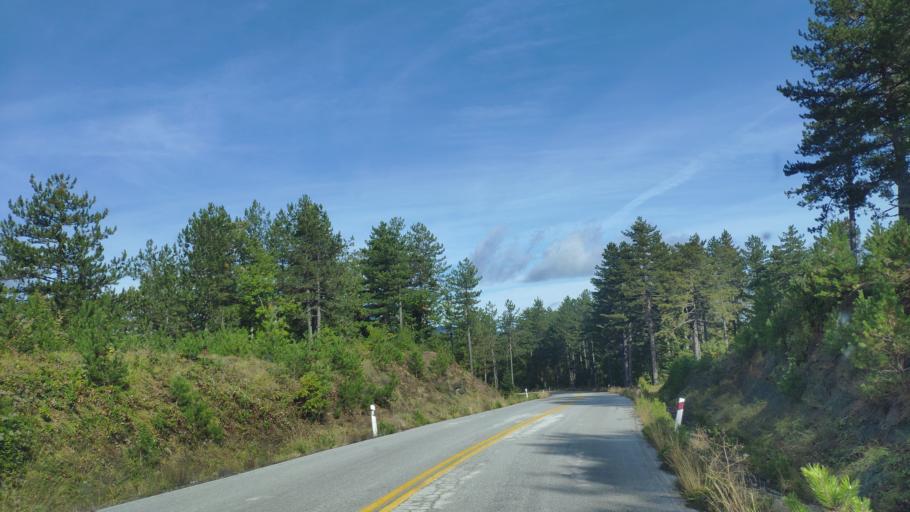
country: GR
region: West Macedonia
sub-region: Nomos Kastorias
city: Nestorio
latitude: 40.3662
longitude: 20.9459
